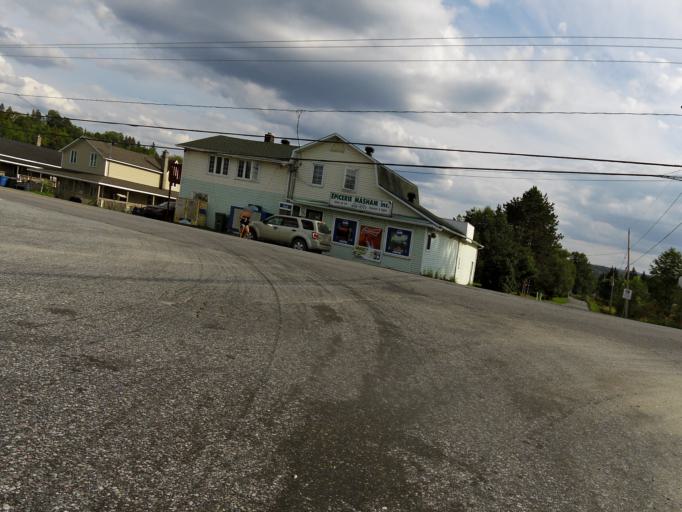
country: CA
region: Quebec
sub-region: Outaouais
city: Wakefield
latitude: 45.6446
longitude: -76.0148
